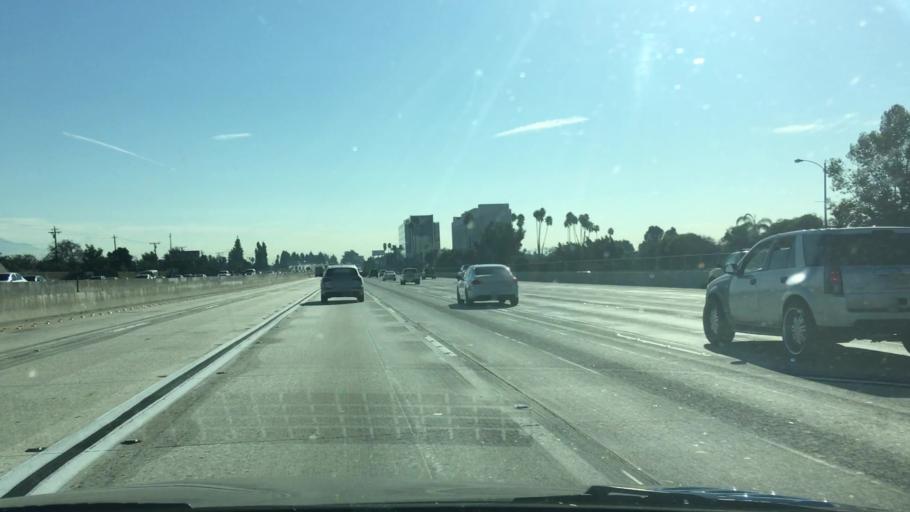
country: US
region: California
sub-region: Los Angeles County
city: Rosemead
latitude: 34.0723
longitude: -118.0653
